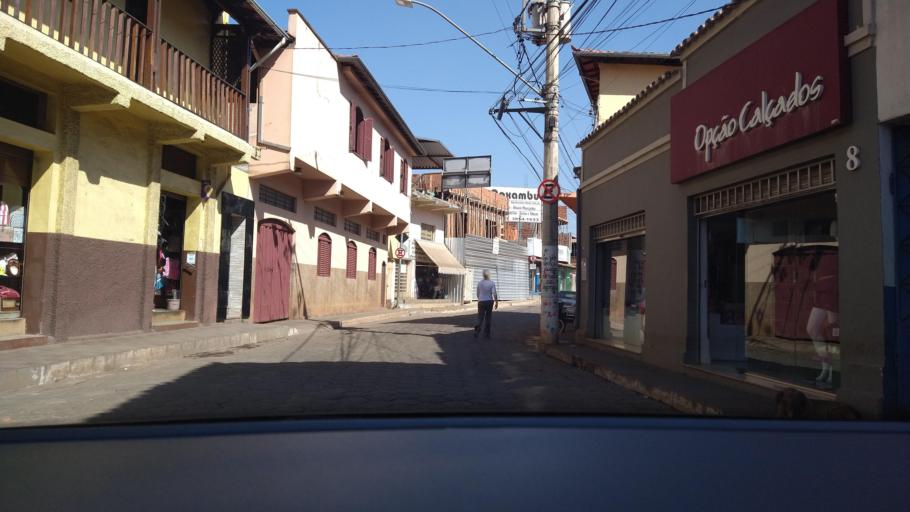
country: BR
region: Minas Gerais
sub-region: Rio Piracicaba
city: Rio Piracicaba
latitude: -19.9315
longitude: -43.1745
